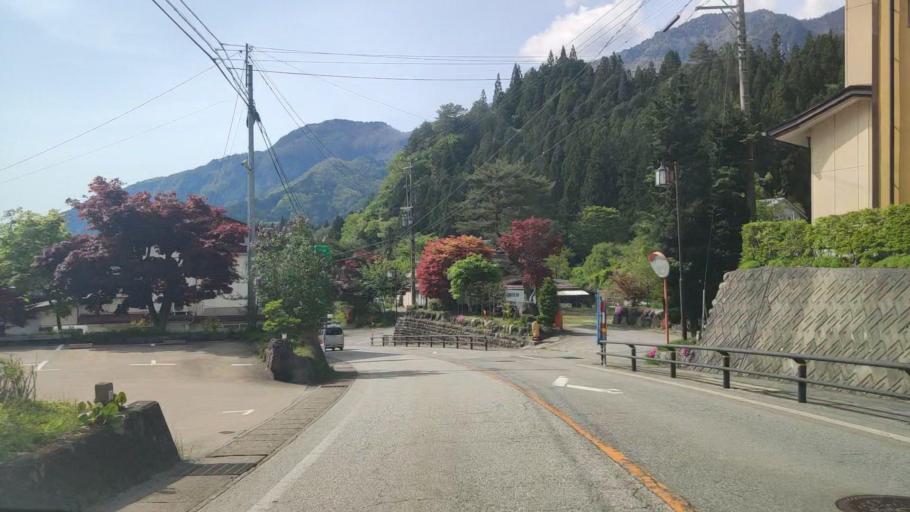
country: JP
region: Gifu
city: Takayama
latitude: 36.2394
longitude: 137.5281
